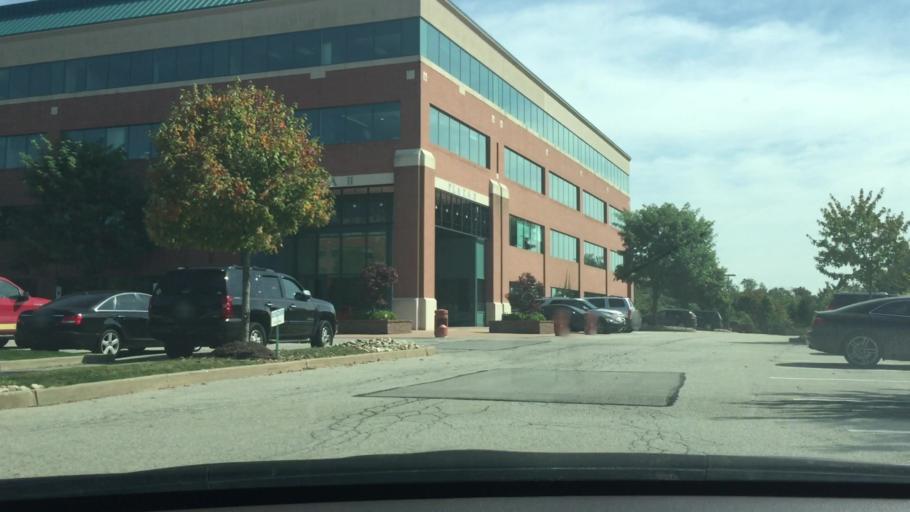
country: US
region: Pennsylvania
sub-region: Washington County
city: Muse
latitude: 40.2950
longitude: -80.1733
